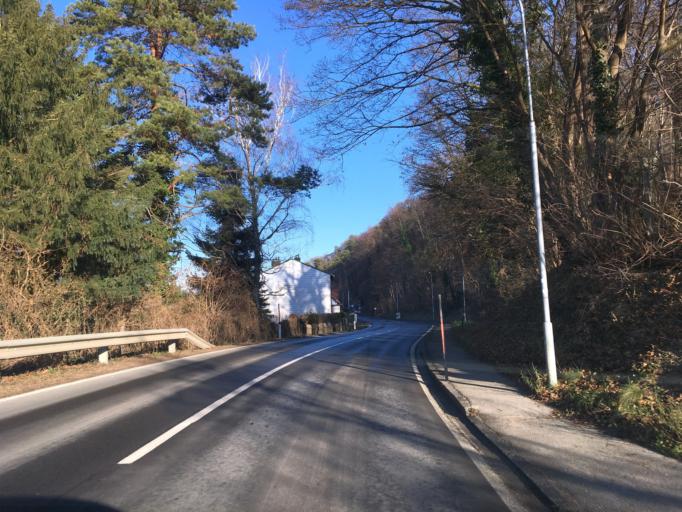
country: AT
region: Lower Austria
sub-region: Politischer Bezirk Tulln
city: Wordern
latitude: 48.3332
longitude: 16.2248
